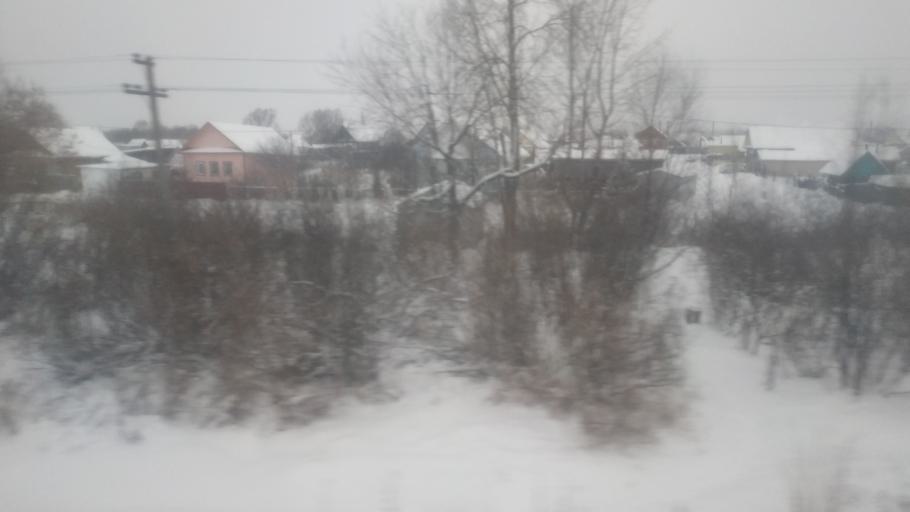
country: RU
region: Bashkortostan
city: Yanaul
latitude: 56.2787
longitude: 54.9513
